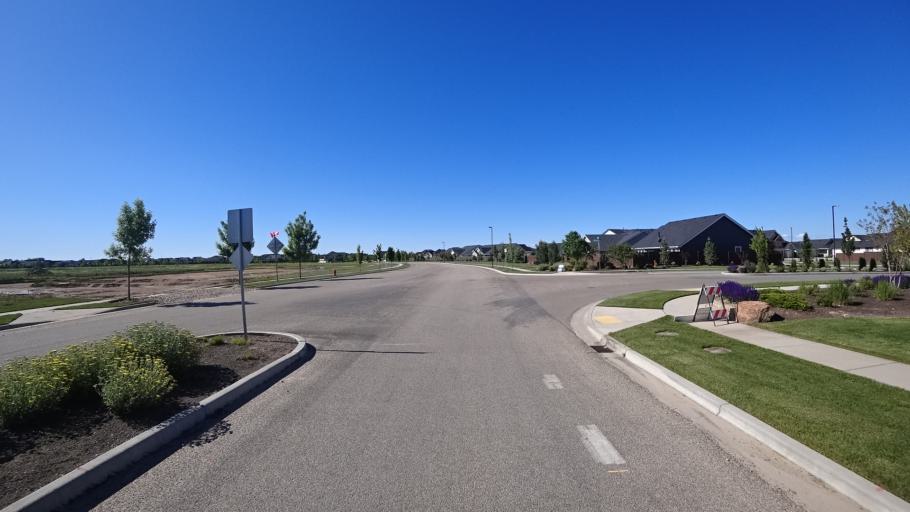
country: US
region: Idaho
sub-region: Ada County
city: Star
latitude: 43.6621
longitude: -116.4438
